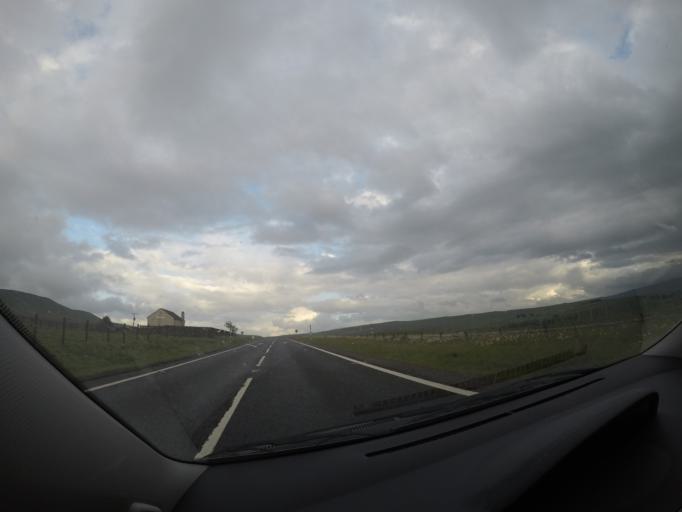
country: GB
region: England
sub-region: Cumbria
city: Kirkby Stephen
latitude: 54.5244
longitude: -2.2277
